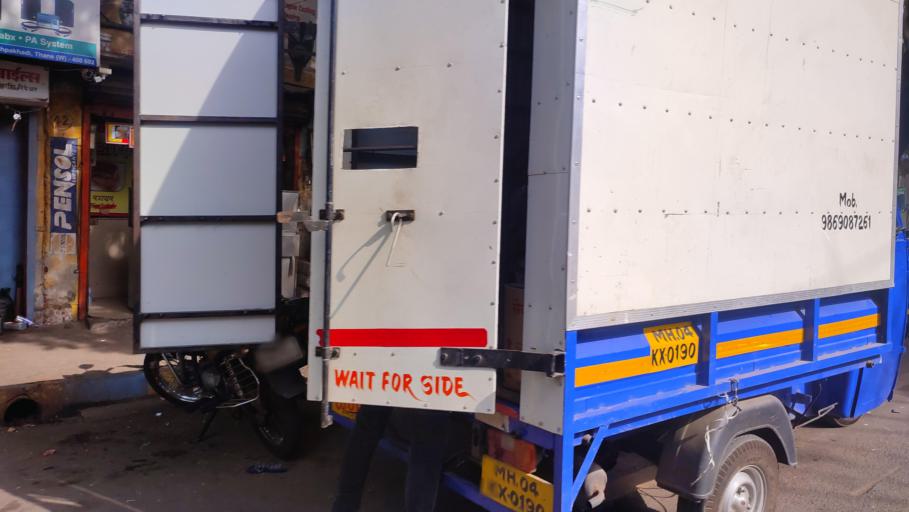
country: IN
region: Maharashtra
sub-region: Thane
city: Thane
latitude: 19.1982
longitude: 72.9633
